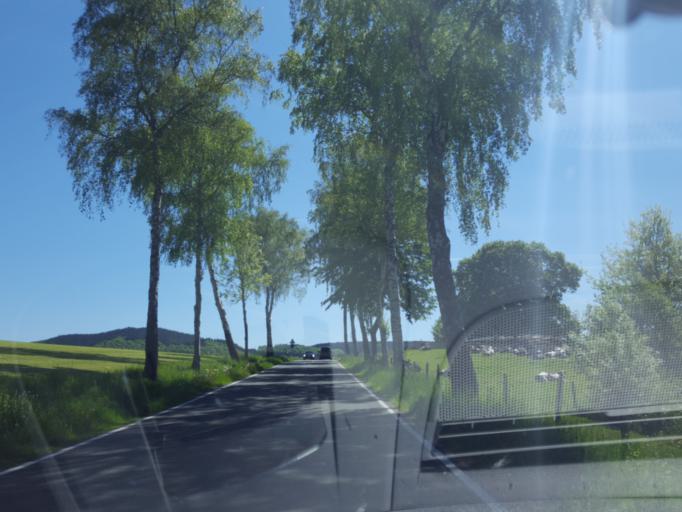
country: DE
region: North Rhine-Westphalia
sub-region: Regierungsbezirk Arnsberg
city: Olsberg
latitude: 51.2666
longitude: 8.4592
